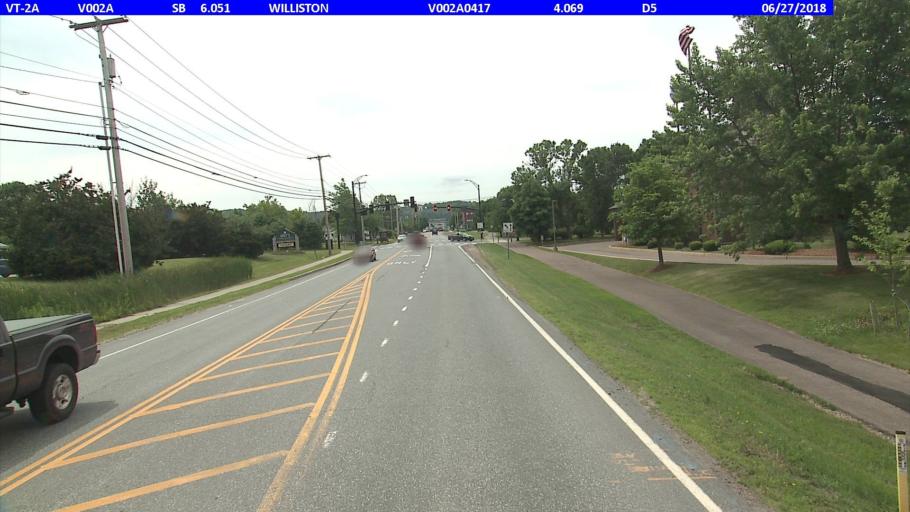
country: US
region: Vermont
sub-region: Chittenden County
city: Essex Junction
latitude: 44.4546
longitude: -73.1116
